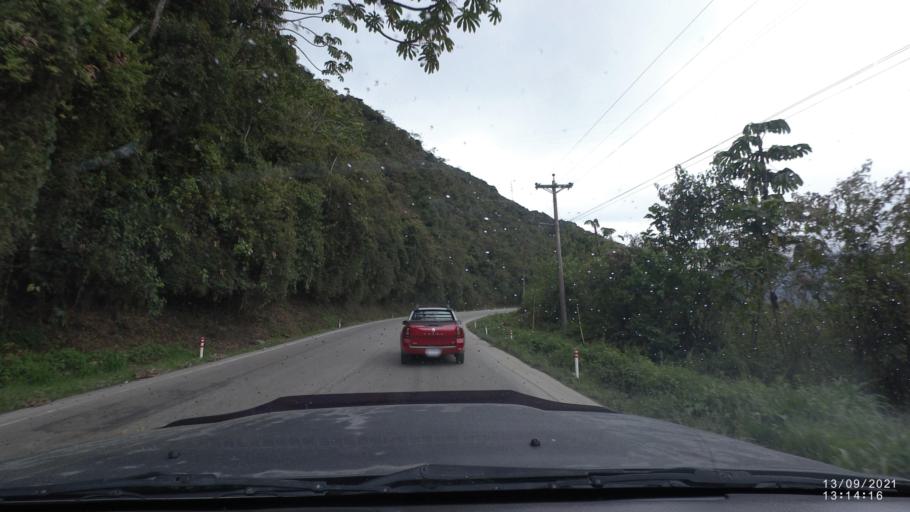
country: BO
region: Cochabamba
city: Colomi
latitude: -17.1973
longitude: -65.8485
